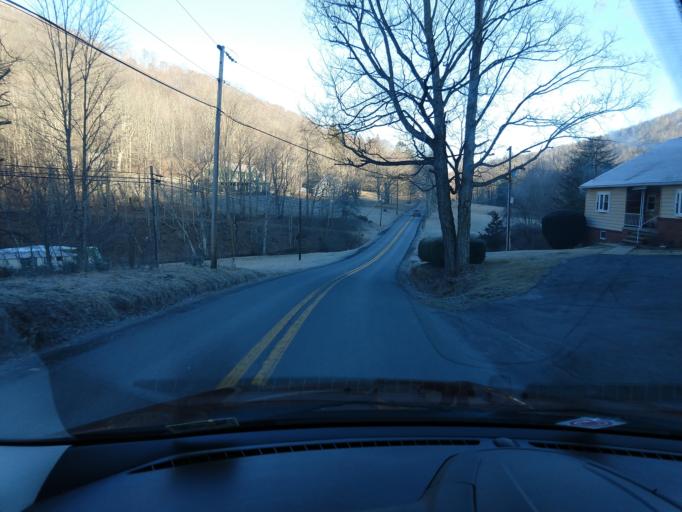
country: US
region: West Virginia
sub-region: Greenbrier County
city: Rainelle
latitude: 37.9473
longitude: -80.7345
